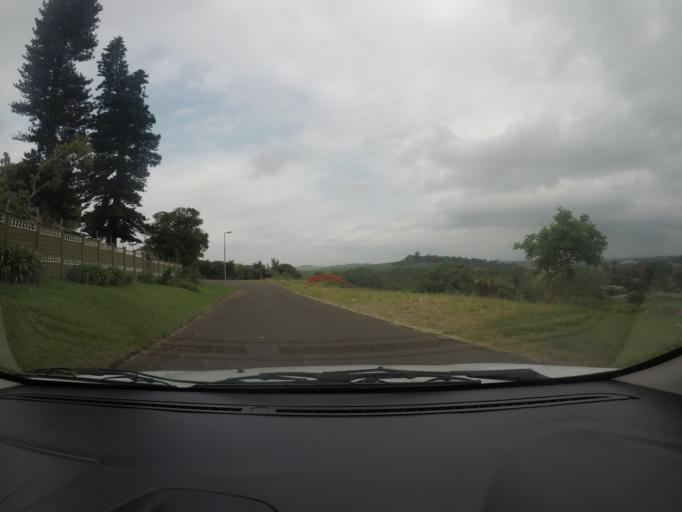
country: ZA
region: KwaZulu-Natal
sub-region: uThungulu District Municipality
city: Empangeni
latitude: -28.7379
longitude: 31.9007
